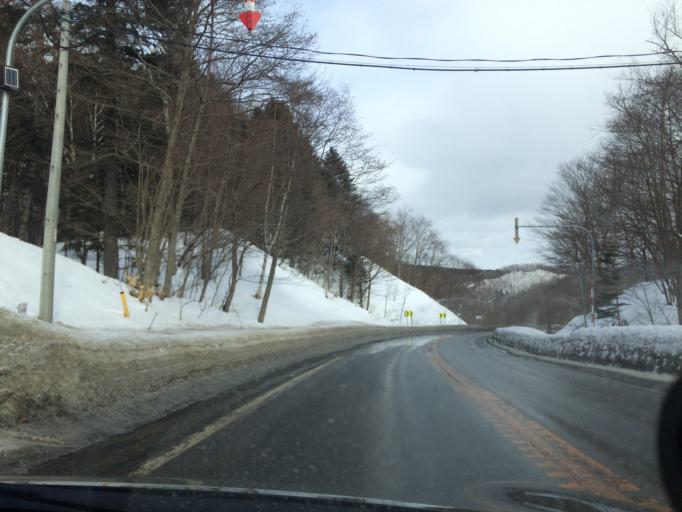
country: JP
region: Hokkaido
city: Shimo-furano
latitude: 42.8847
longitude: 142.2337
